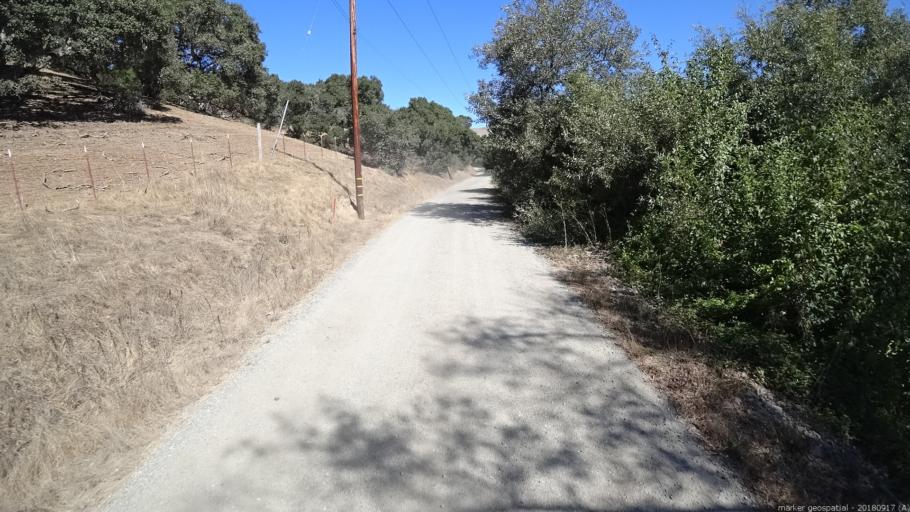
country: US
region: California
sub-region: San Benito County
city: San Juan Bautista
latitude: 36.8018
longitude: -121.5656
